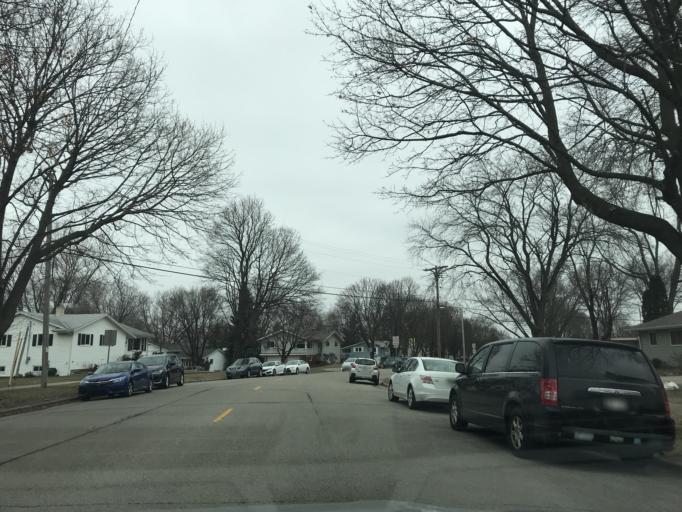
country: US
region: Wisconsin
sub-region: Dane County
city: Monona
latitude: 43.0931
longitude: -89.2980
